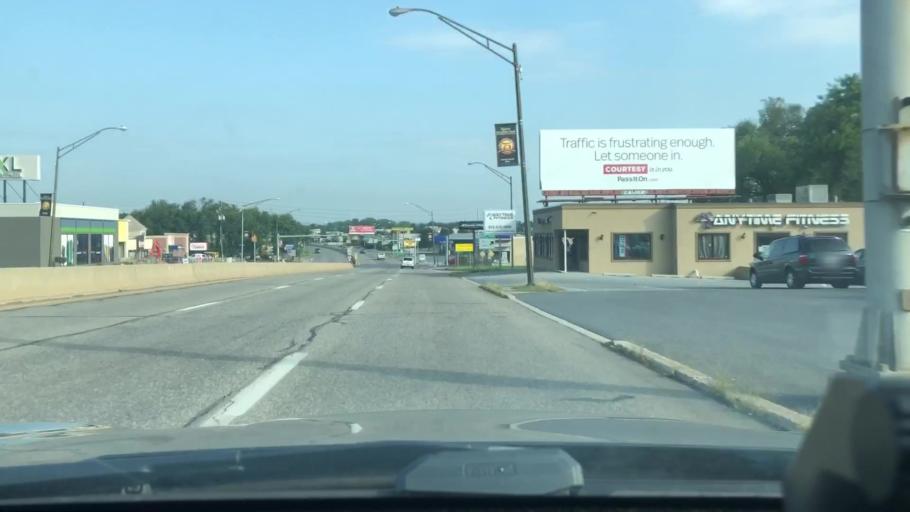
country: US
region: Pennsylvania
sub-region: Lehigh County
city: Fullerton
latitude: 40.6404
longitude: -75.4897
